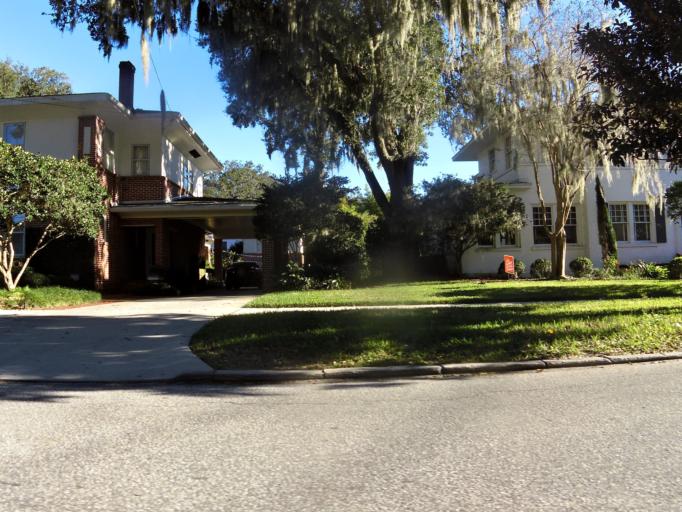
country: US
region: Florida
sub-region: Duval County
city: Jacksonville
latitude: 30.2986
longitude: -81.7033
